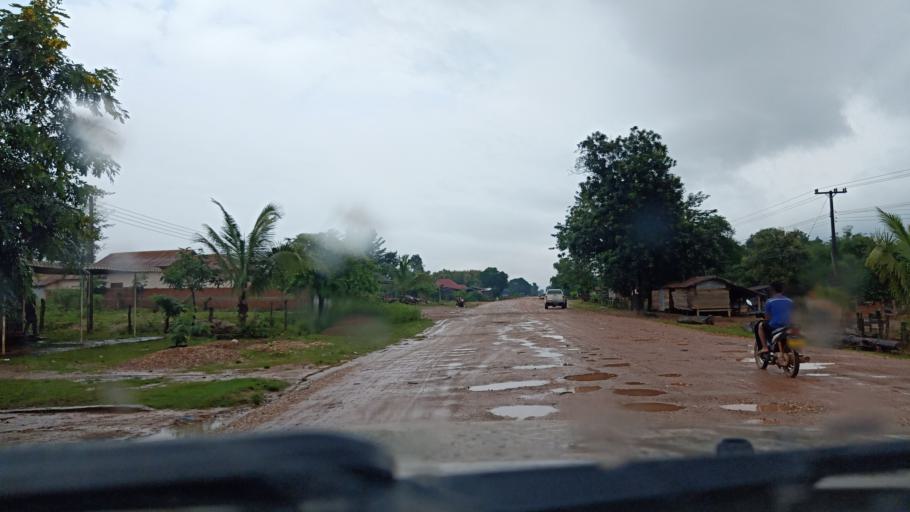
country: LA
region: Attapu
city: Attapu
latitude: 14.7123
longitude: 106.6622
